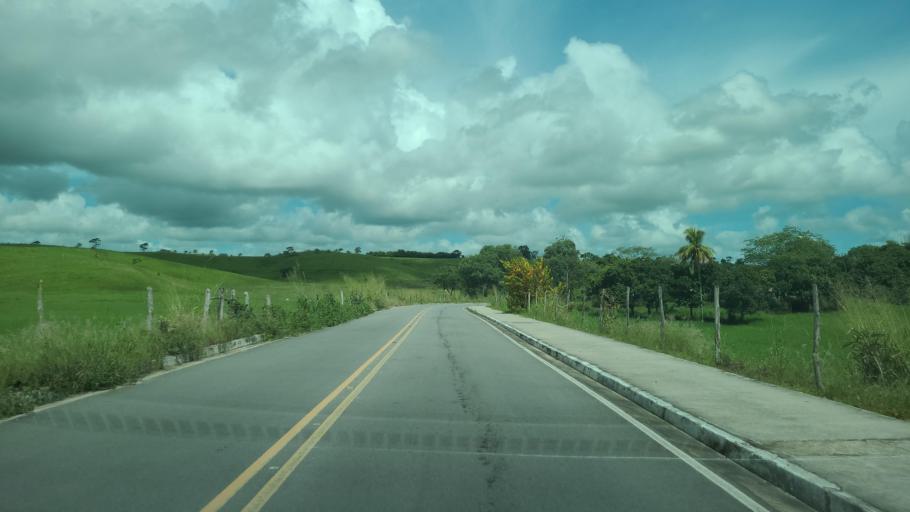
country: BR
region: Alagoas
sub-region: Uniao Dos Palmares
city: Uniao dos Palmares
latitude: -9.1619
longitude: -36.0478
